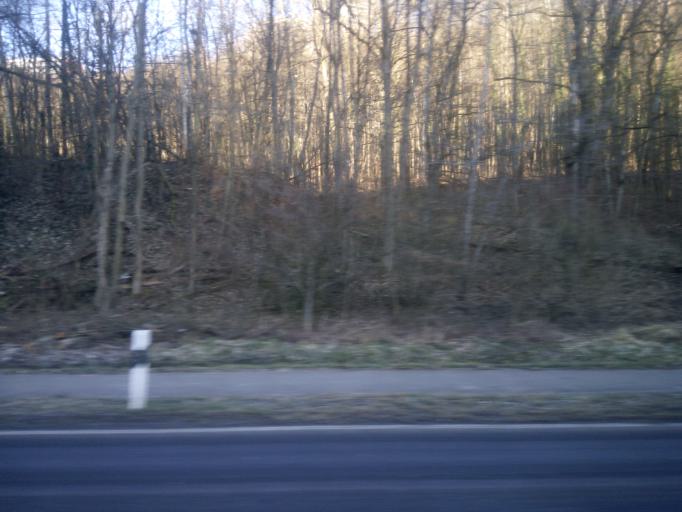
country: LU
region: Luxembourg
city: Kirchberg
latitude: 49.6384
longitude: 6.1498
